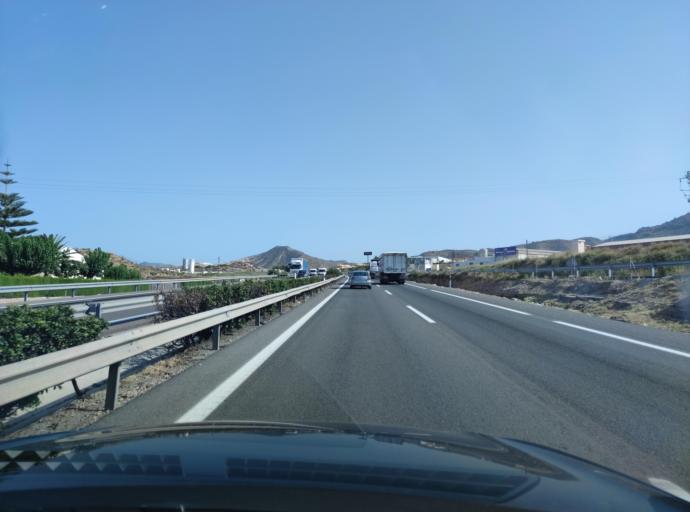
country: ES
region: Valencia
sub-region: Provincia de Alicante
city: Novelda
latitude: 38.4163
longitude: -0.7809
